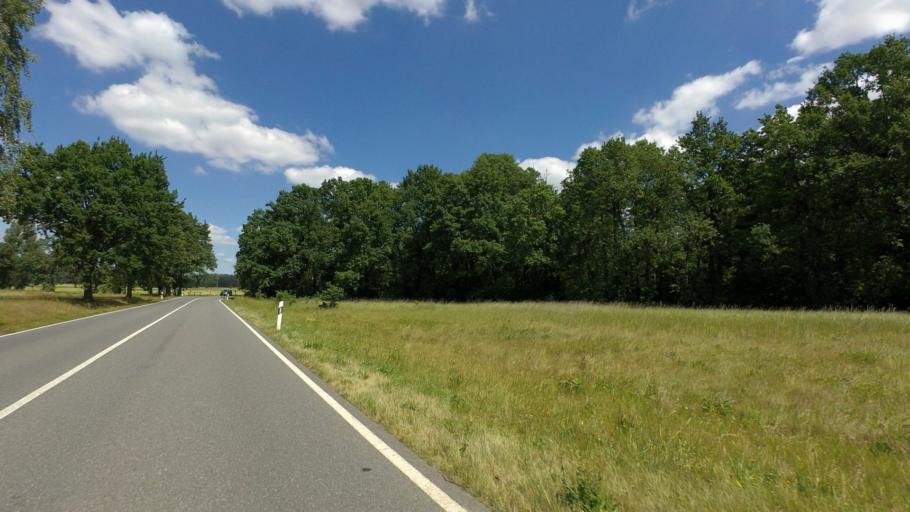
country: DE
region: Brandenburg
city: Luckau
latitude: 51.7829
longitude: 13.6881
